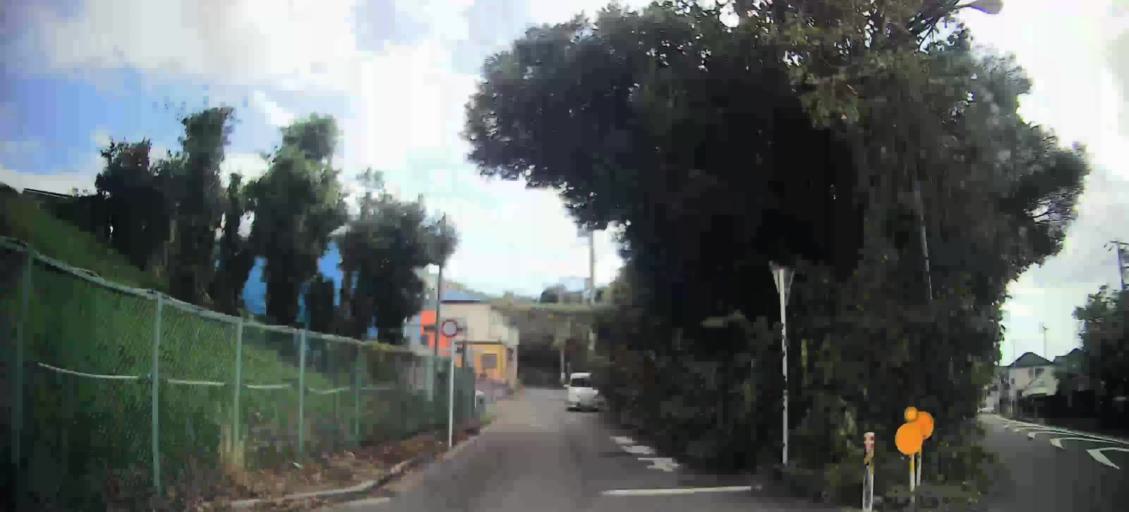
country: JP
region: Kanagawa
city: Yokohama
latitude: 35.4855
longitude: 139.5760
